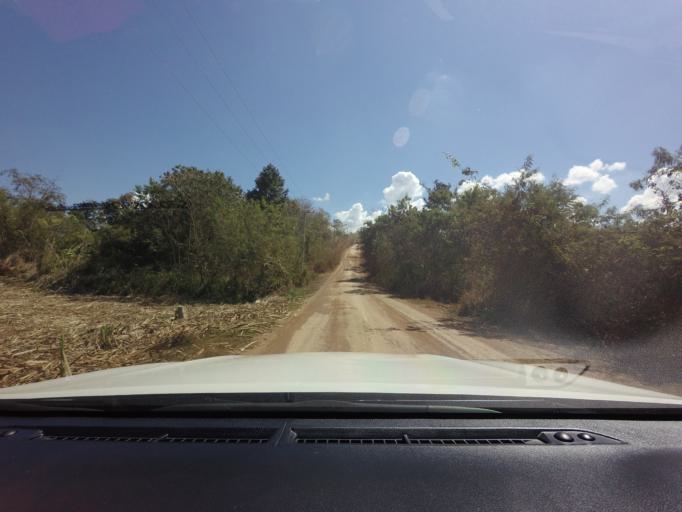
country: TH
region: Nakhon Ratchasima
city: Wang Nam Khiao
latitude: 14.4444
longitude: 101.6894
